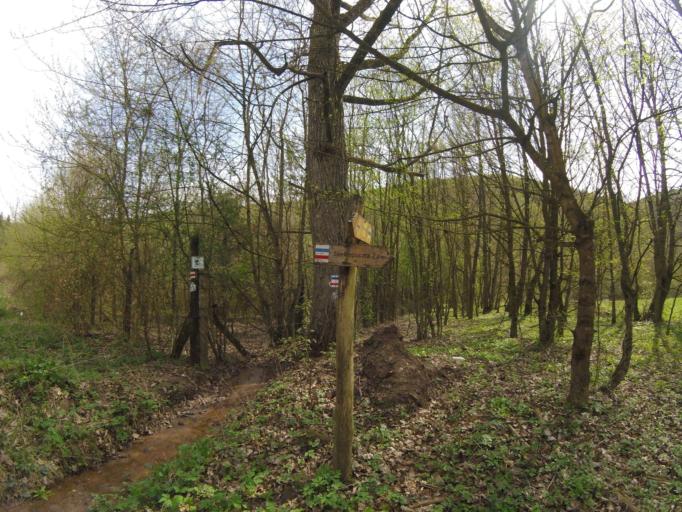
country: HU
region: Borsod-Abauj-Zemplen
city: Rudabanya
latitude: 48.5307
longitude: 20.6271
